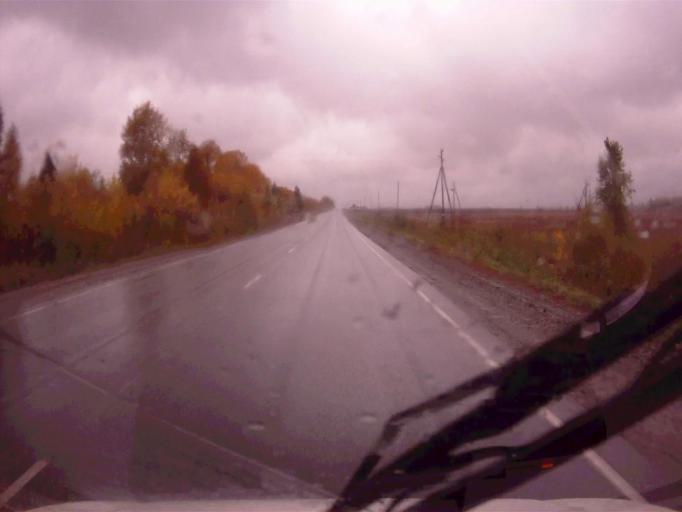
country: RU
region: Chelyabinsk
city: Argayash
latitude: 55.4249
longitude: 61.0054
